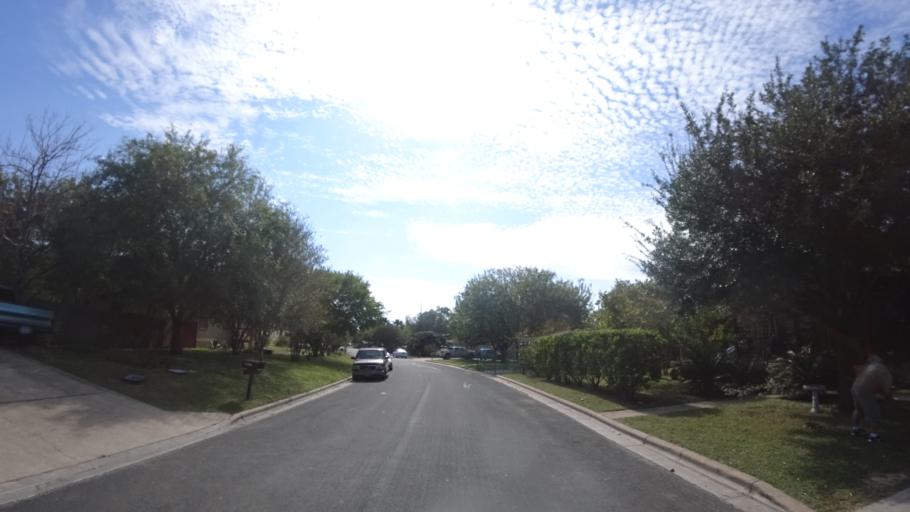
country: US
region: Texas
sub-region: Travis County
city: Pflugerville
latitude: 30.4103
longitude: -97.6331
